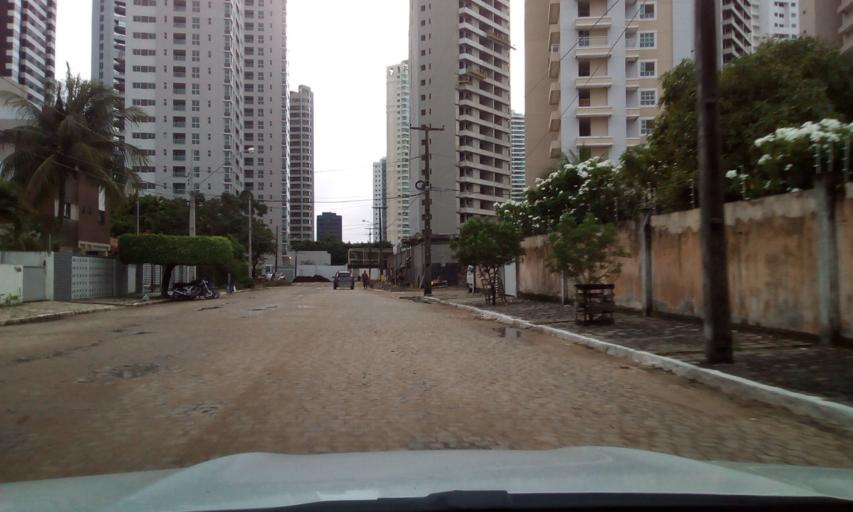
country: BR
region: Paraiba
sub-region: Joao Pessoa
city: Joao Pessoa
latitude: -7.1336
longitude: -34.8284
